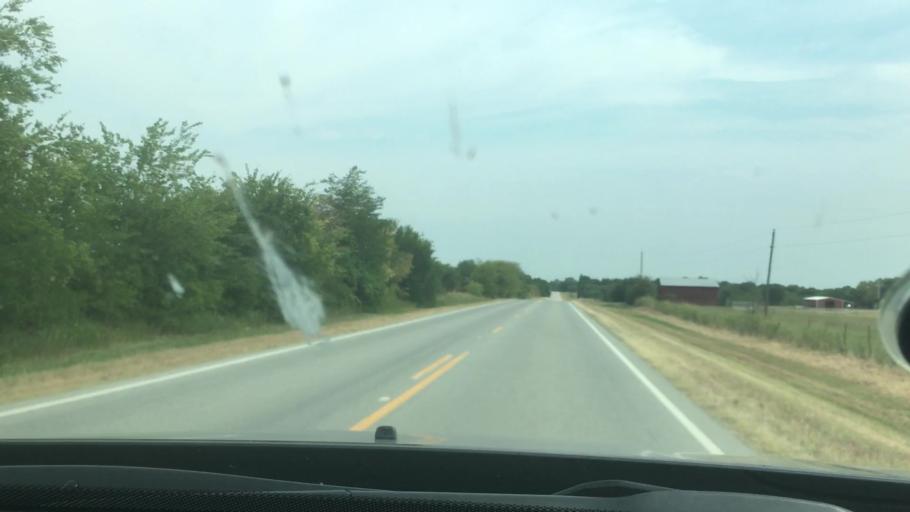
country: US
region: Oklahoma
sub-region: Coal County
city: Coalgate
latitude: 34.5204
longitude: -96.4070
